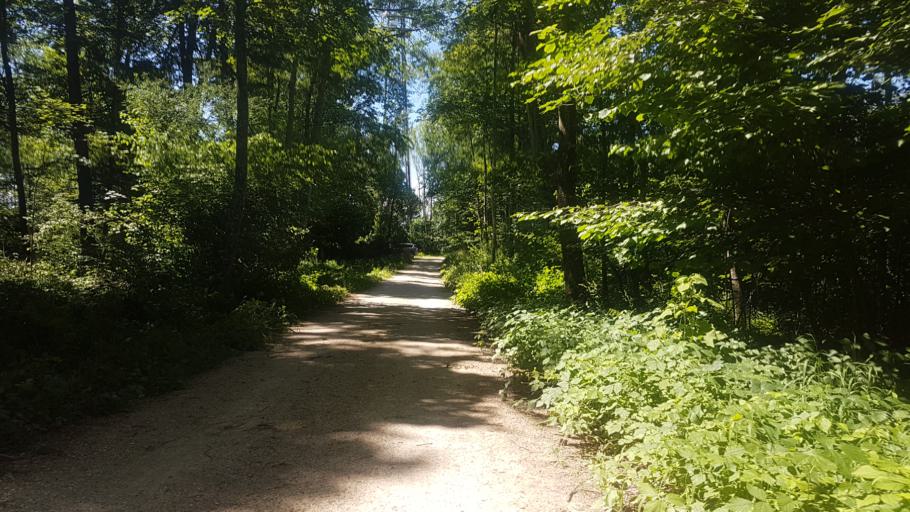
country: DE
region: Bavaria
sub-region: Upper Bavaria
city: Weichering
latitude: 48.7278
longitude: 11.3136
